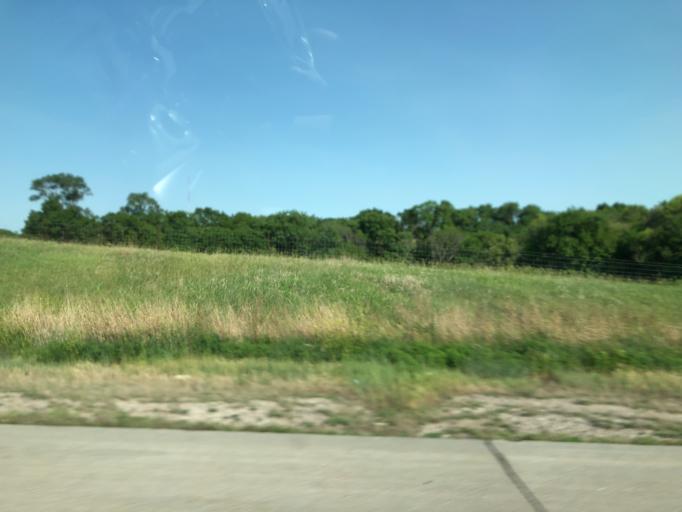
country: US
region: Nebraska
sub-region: Sarpy County
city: Gretna
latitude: 41.0793
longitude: -96.2790
